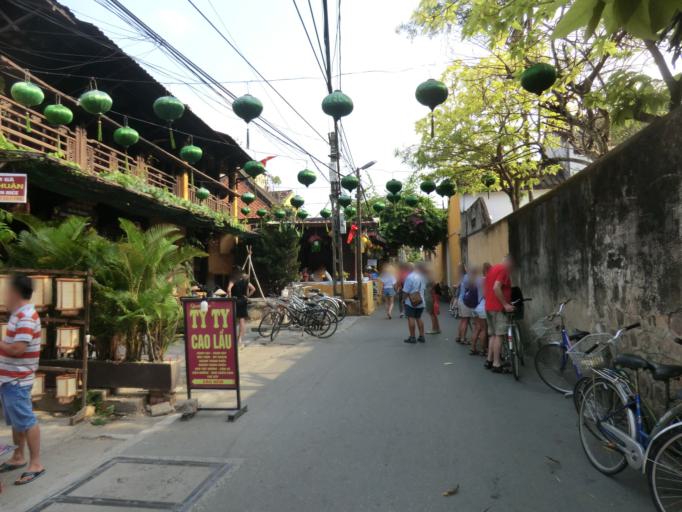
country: VN
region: Quang Nam
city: Hoi An
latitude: 15.8777
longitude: 108.3268
